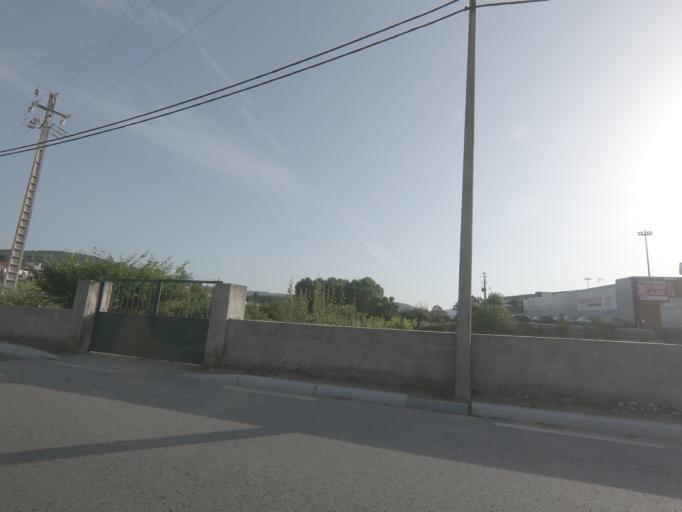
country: PT
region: Vila Real
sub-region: Sabrosa
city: Sabrosa
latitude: 41.2696
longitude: -7.4763
